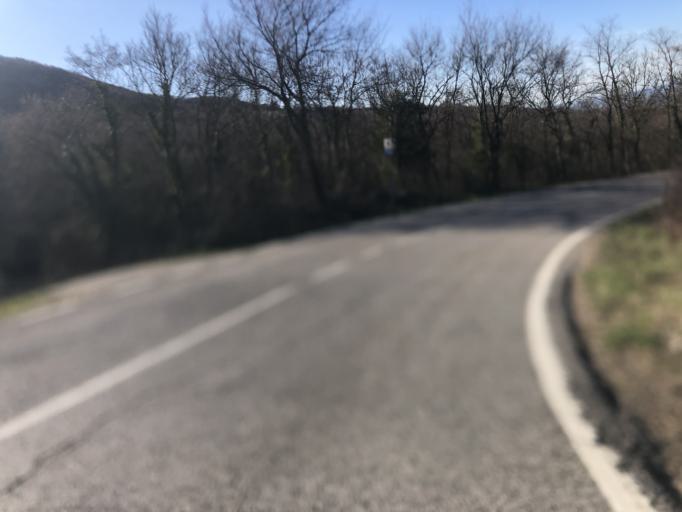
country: IT
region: Veneto
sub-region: Provincia di Verona
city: Fumane
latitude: 45.5609
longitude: 10.8514
